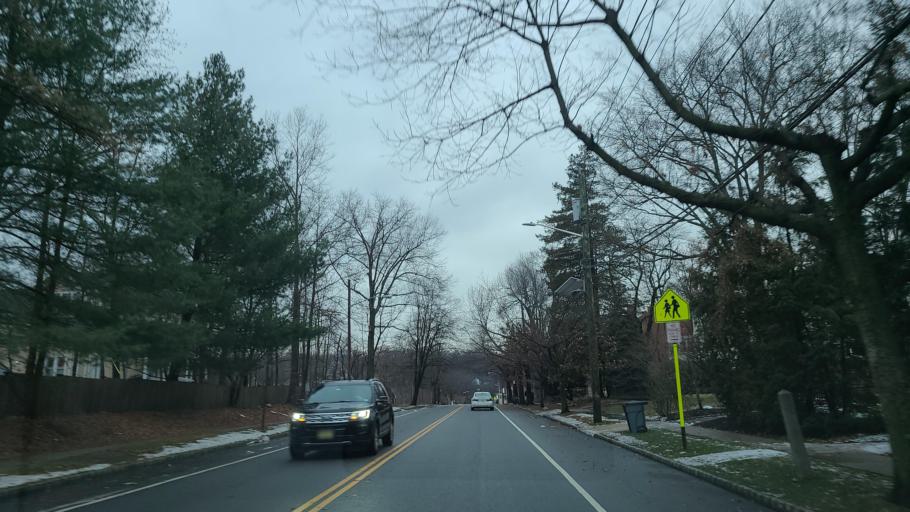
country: US
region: New Jersey
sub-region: Essex County
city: Upper Montclair
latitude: 40.8399
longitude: -74.2016
